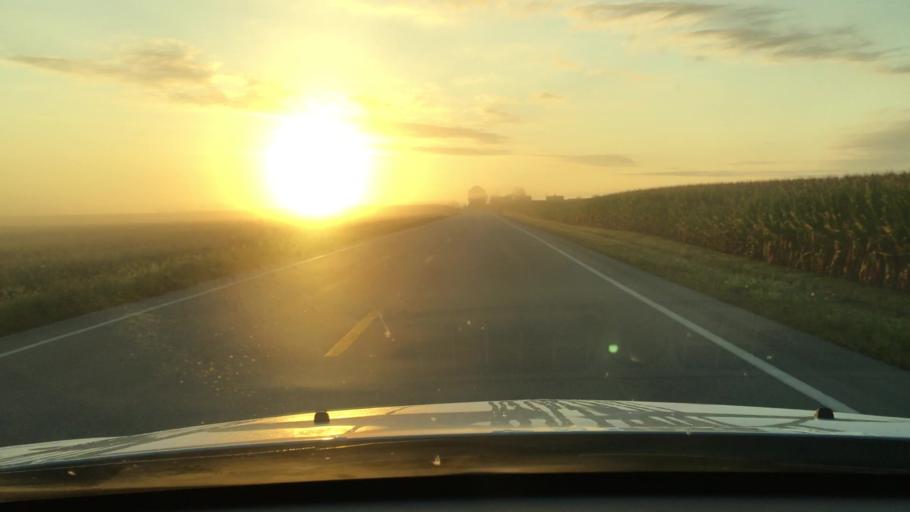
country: US
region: Illinois
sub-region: DeKalb County
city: Waterman
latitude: 41.8492
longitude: -88.8136
